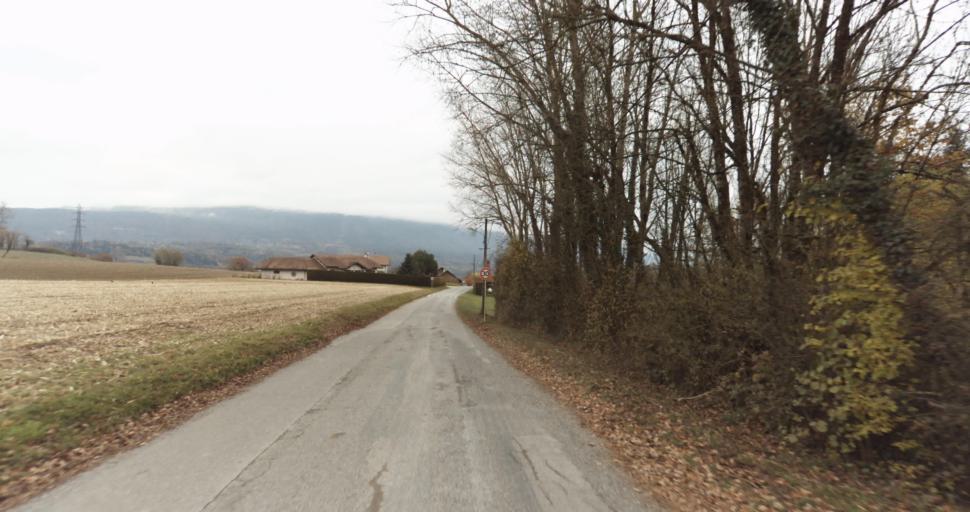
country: FR
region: Rhone-Alpes
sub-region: Departement de la Haute-Savoie
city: Chavanod
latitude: 45.8566
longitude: 6.0444
